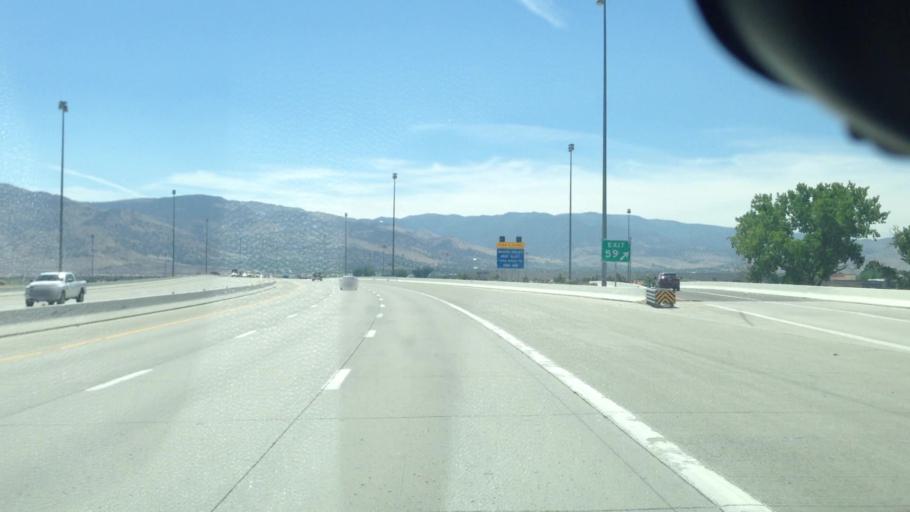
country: US
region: Nevada
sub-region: Washoe County
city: Sparks
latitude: 39.4254
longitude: -119.7551
